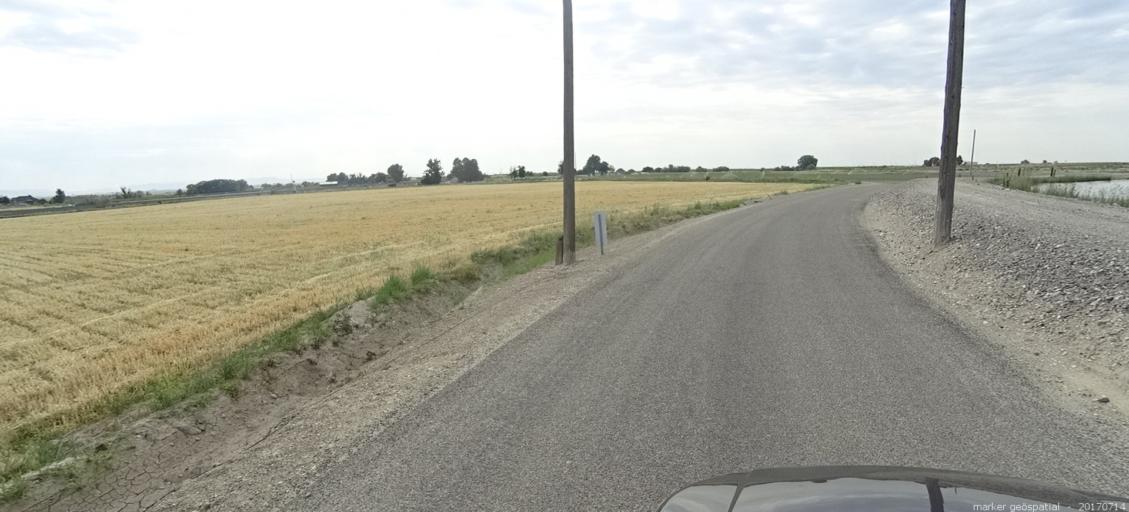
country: US
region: Idaho
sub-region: Ada County
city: Kuna
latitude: 43.4601
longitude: -116.3643
